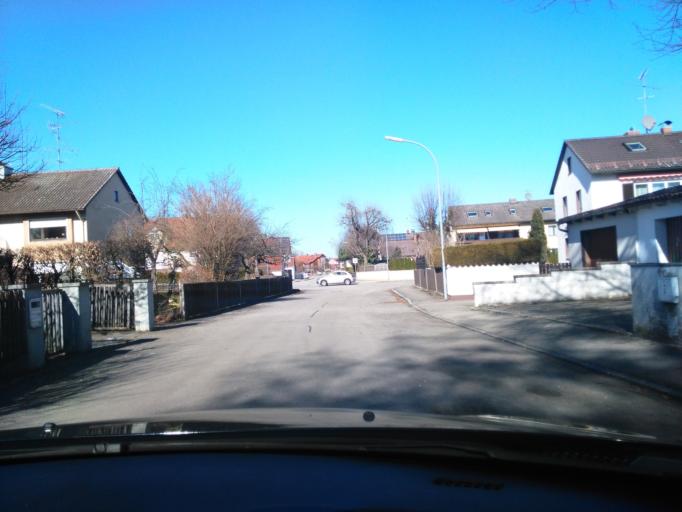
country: DE
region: Bavaria
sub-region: Upper Bavaria
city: Mammendorf
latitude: 48.2094
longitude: 11.1719
